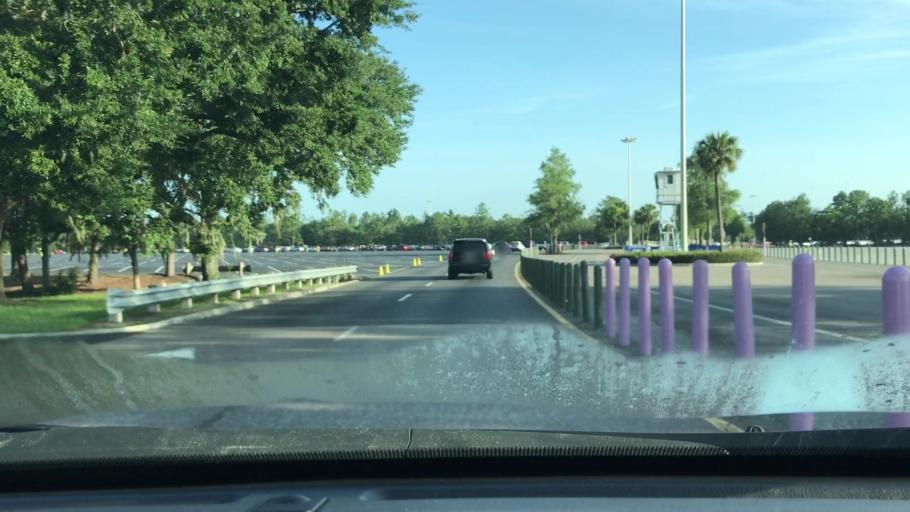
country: US
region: Florida
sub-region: Osceola County
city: Celebration
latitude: 28.3992
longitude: -81.5815
